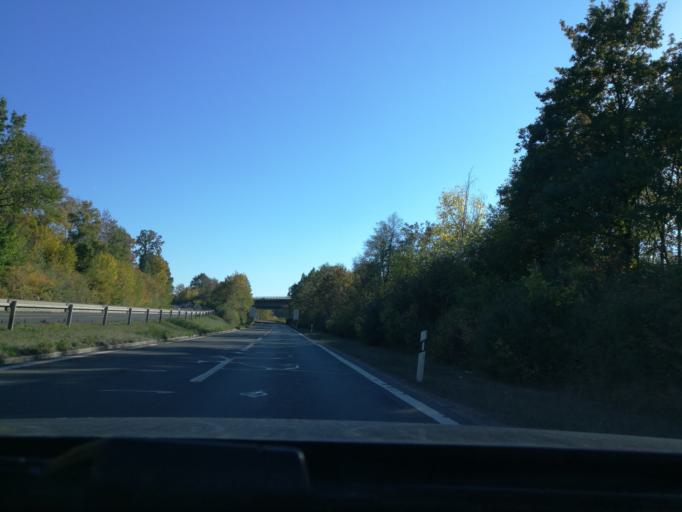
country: DE
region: Bavaria
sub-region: Regierungsbezirk Mittelfranken
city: Zirndorf
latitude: 49.4780
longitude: 10.9444
